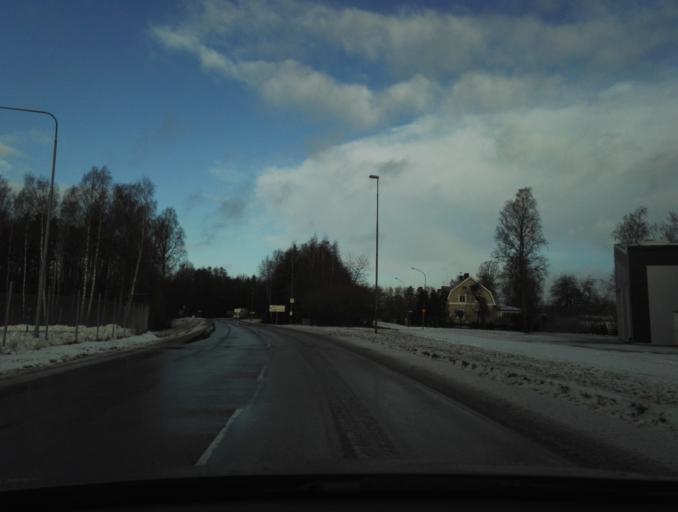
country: SE
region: Kronoberg
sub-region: Vaxjo Kommun
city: Vaexjoe
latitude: 56.8874
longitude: 14.7357
